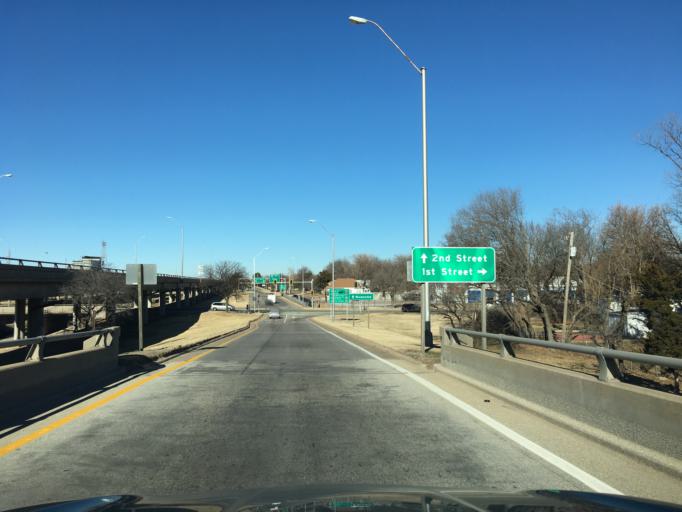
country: US
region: Kansas
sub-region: Sedgwick County
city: Wichita
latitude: 37.6869
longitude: -97.3128
